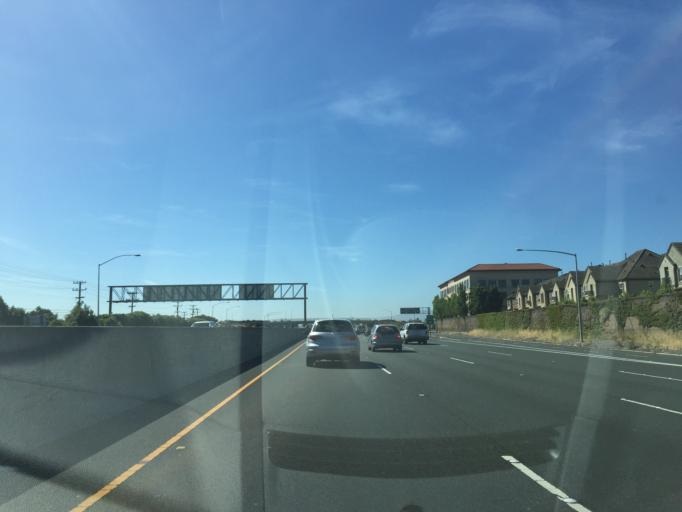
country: US
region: California
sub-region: San Mateo County
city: Foster City
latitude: 37.5479
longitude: -122.2911
